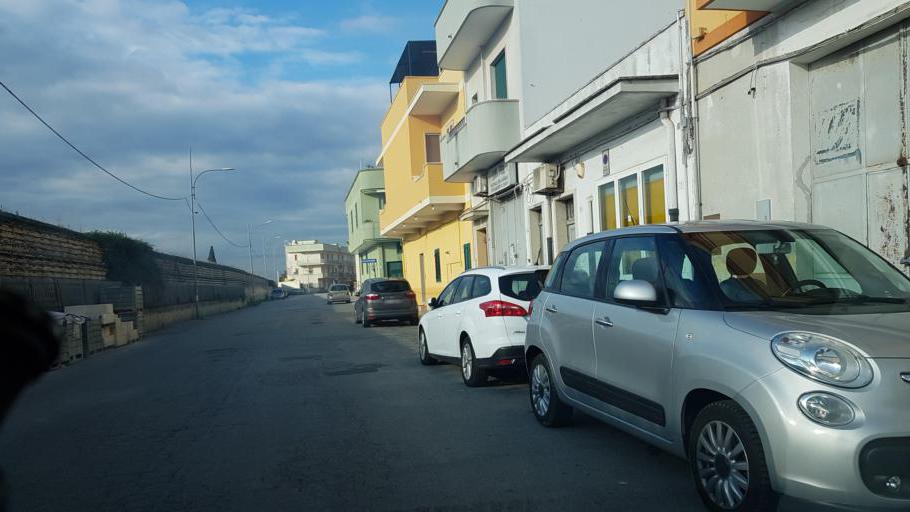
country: IT
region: Apulia
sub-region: Provincia di Brindisi
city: Francavilla Fontana
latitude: 40.5265
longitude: 17.5771
